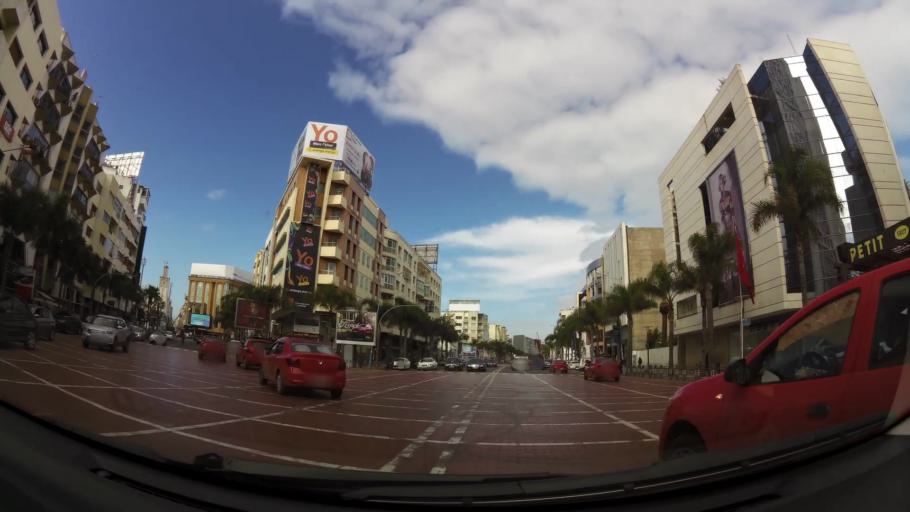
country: MA
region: Grand Casablanca
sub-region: Casablanca
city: Casablanca
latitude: 33.5869
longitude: -7.6336
